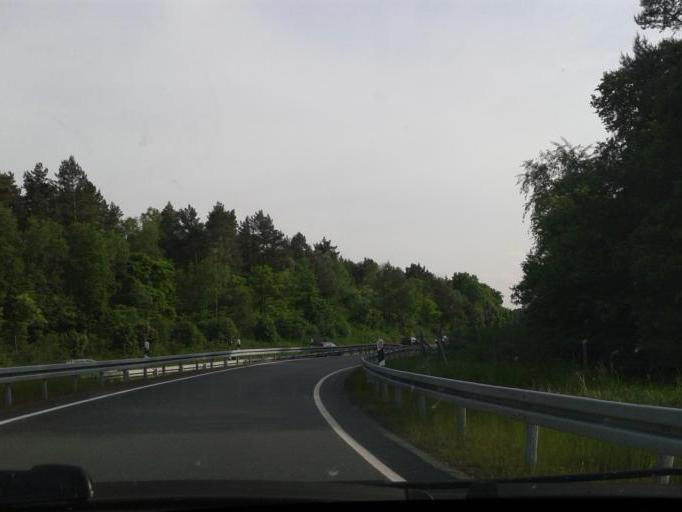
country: DE
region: North Rhine-Westphalia
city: Bad Lippspringe
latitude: 51.7787
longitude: 8.7783
